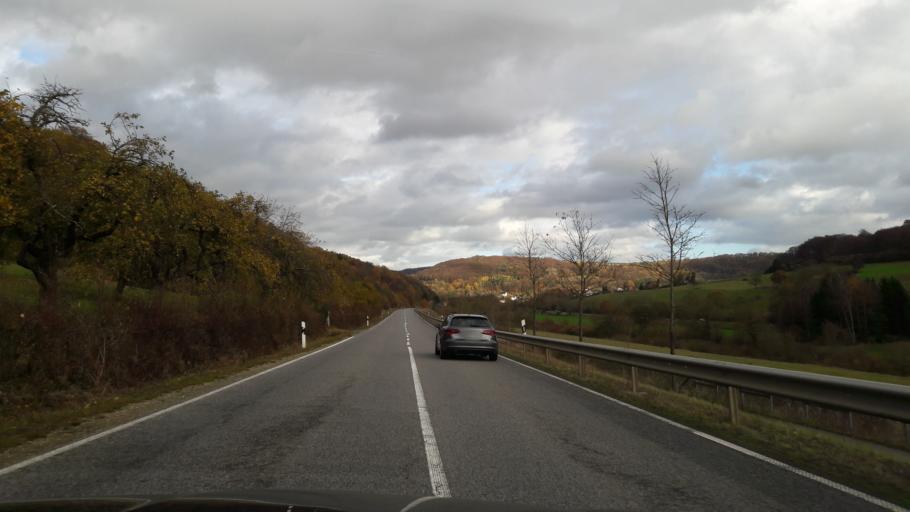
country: DE
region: Rheinland-Pfalz
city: Echternacherbruck
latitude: 49.8139
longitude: 6.4554
